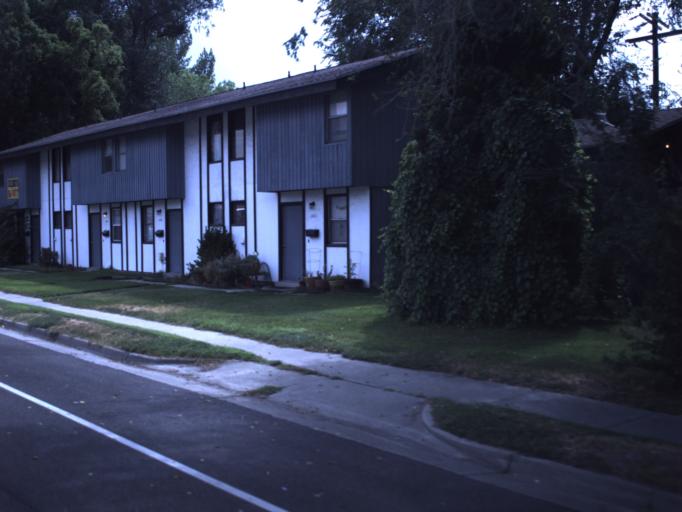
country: US
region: Utah
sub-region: Salt Lake County
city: South Salt Lake
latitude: 40.7311
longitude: -111.8713
